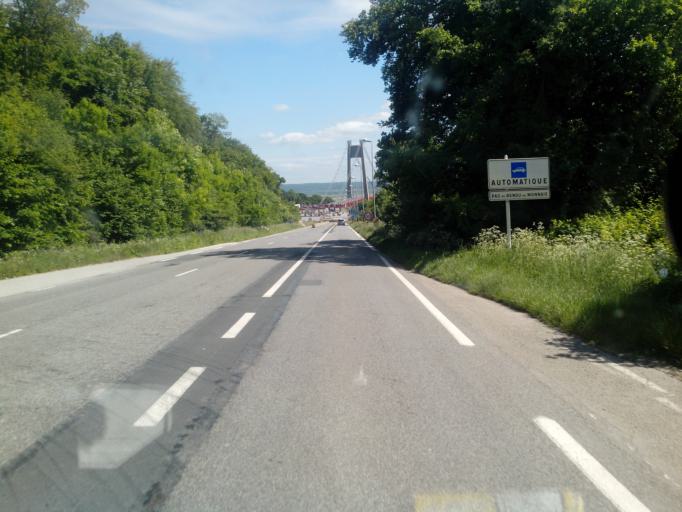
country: FR
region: Haute-Normandie
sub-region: Departement de la Seine-Maritime
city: Tancarville
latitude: 49.4804
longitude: 0.4543
